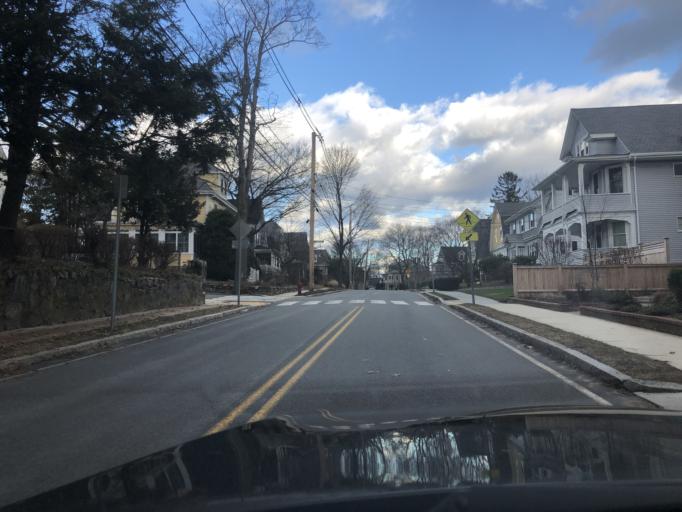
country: US
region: Massachusetts
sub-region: Middlesex County
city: Arlington
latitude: 42.4107
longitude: -71.1631
